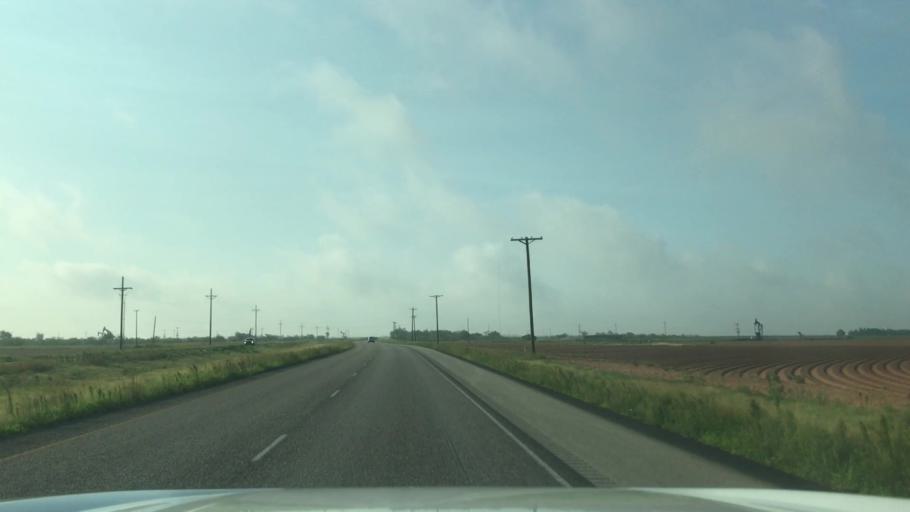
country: US
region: Texas
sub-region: Garza County
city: Post
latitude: 33.2397
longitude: -101.4544
